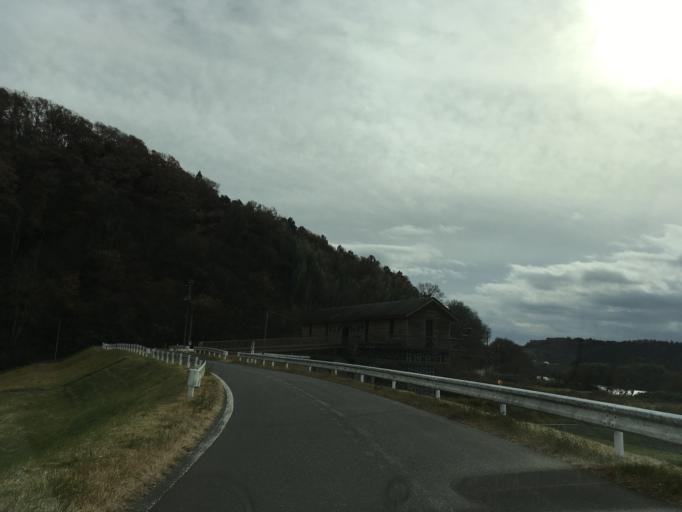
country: JP
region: Iwate
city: Ichinoseki
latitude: 38.7662
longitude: 141.2742
